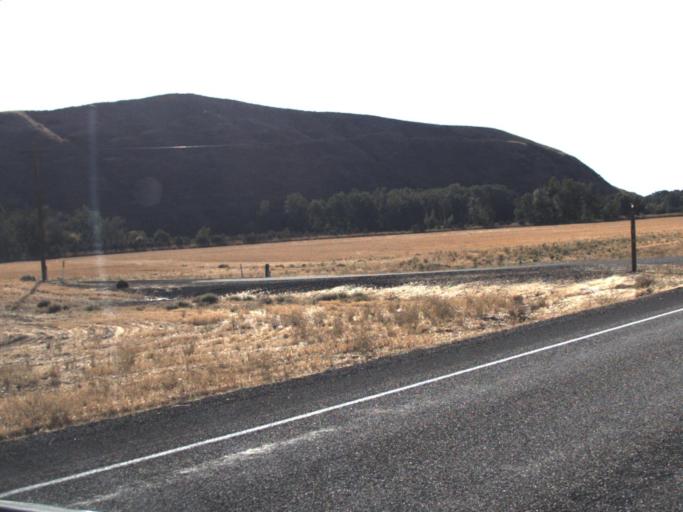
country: US
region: Washington
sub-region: Walla Walla County
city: Waitsburg
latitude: 46.2993
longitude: -118.3498
